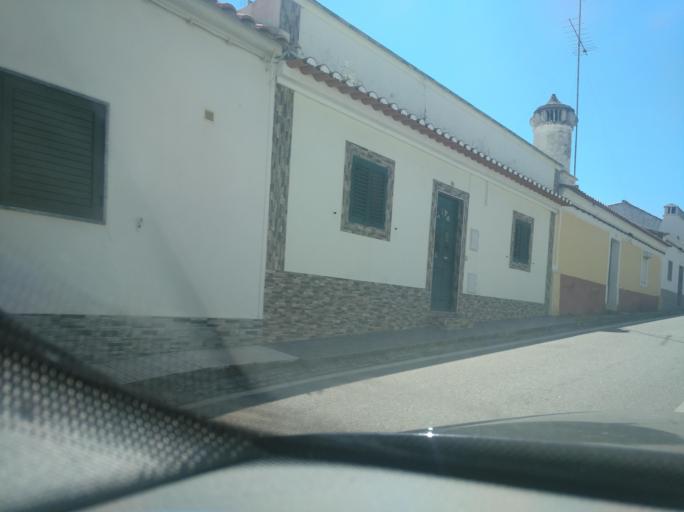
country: PT
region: Portalegre
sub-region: Elvas
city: Elvas
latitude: 38.9614
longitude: -7.2983
